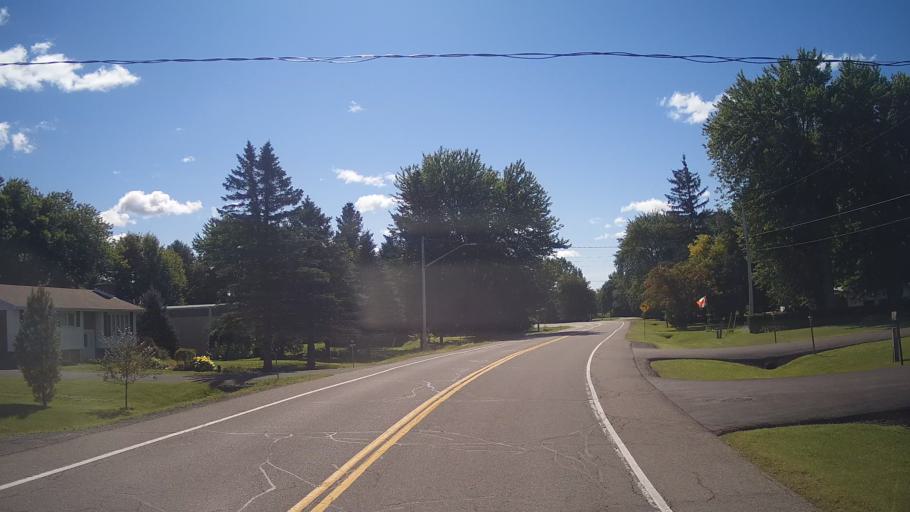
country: US
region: New York
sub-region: St. Lawrence County
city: Norfolk
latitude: 44.9726
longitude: -75.2535
